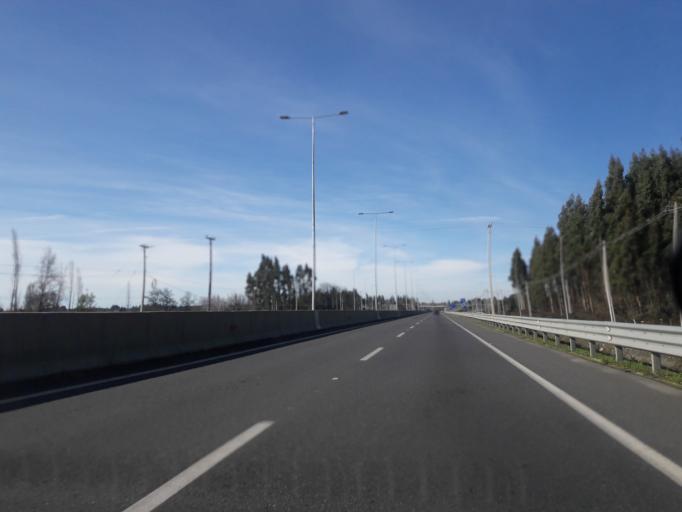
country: CL
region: Biobio
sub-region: Provincia de Biobio
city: Cabrero
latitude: -37.0161
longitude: -72.4973
